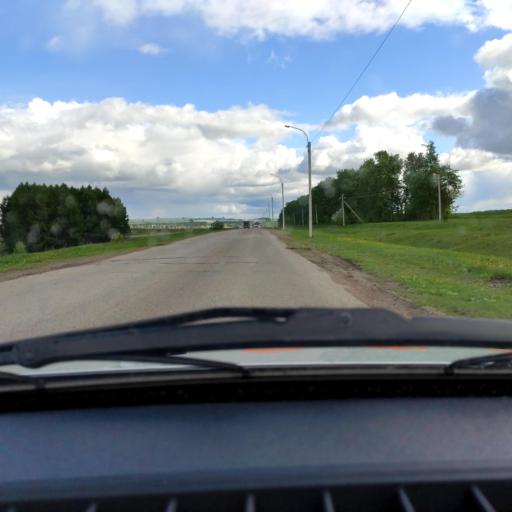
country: RU
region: Bashkortostan
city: Tolbazy
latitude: 53.9696
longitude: 55.9119
